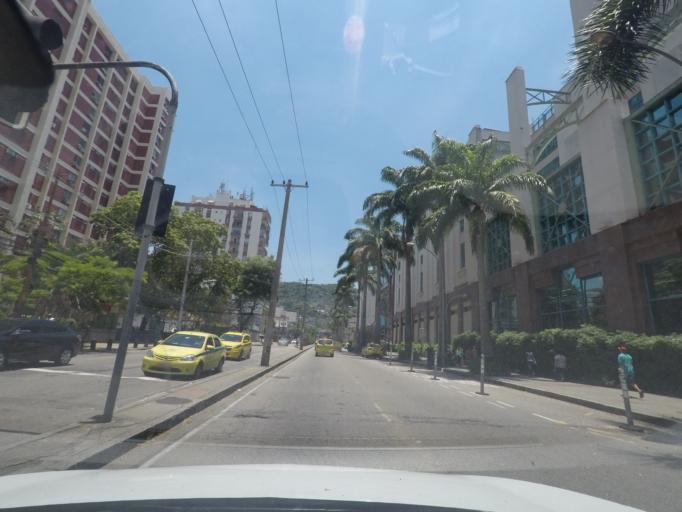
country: BR
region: Rio de Janeiro
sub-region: Rio De Janeiro
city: Rio de Janeiro
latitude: -22.9202
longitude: -43.2506
